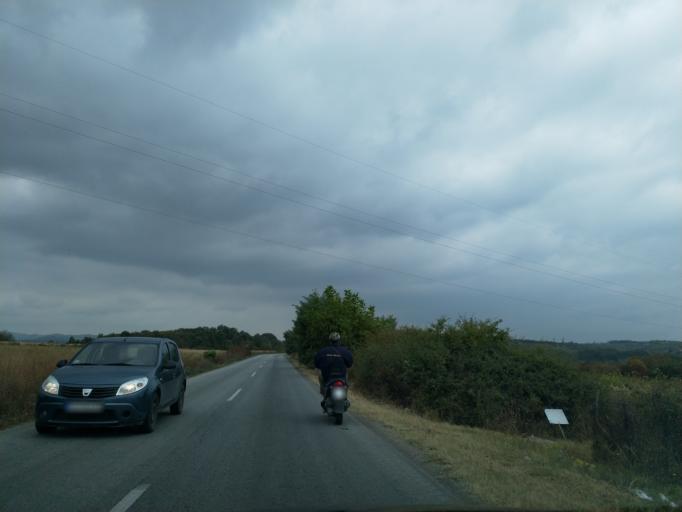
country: RS
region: Central Serbia
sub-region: Pomoravski Okrug
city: Jagodina
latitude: 44.0008
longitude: 21.2136
